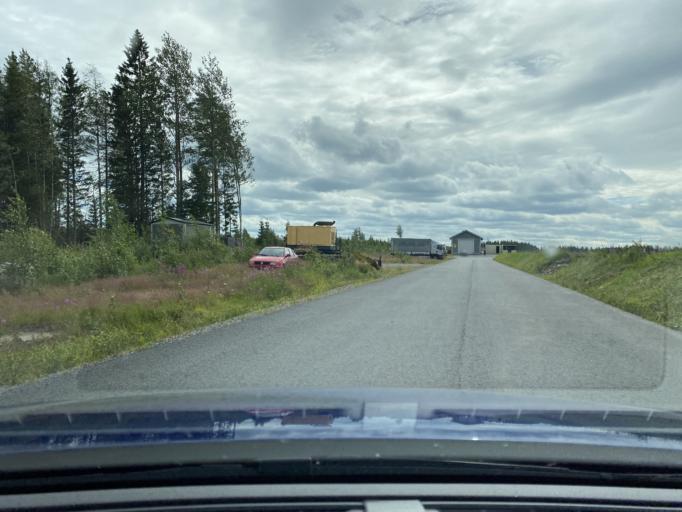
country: FI
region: Southern Ostrobothnia
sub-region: Seinaejoki
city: Jurva
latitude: 62.6242
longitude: 22.0327
